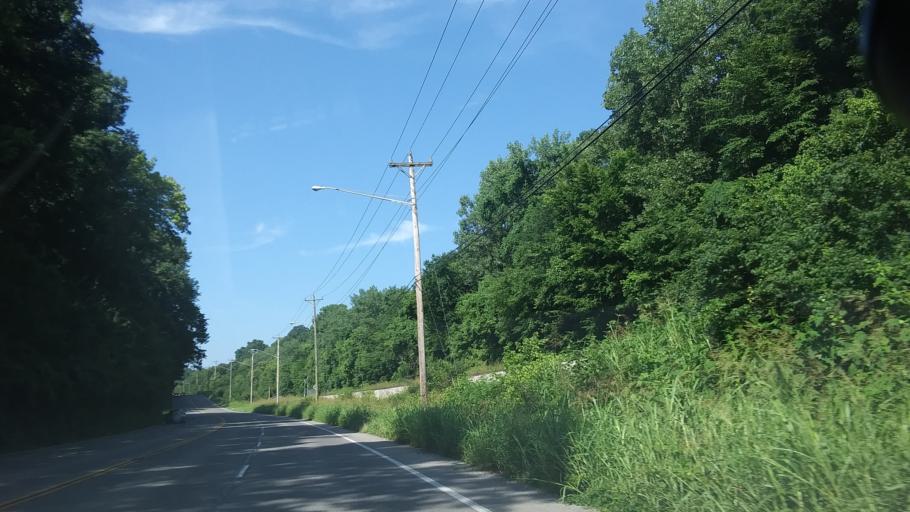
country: US
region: Tennessee
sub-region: Davidson County
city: Belle Meade
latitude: 36.0749
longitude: -86.8915
